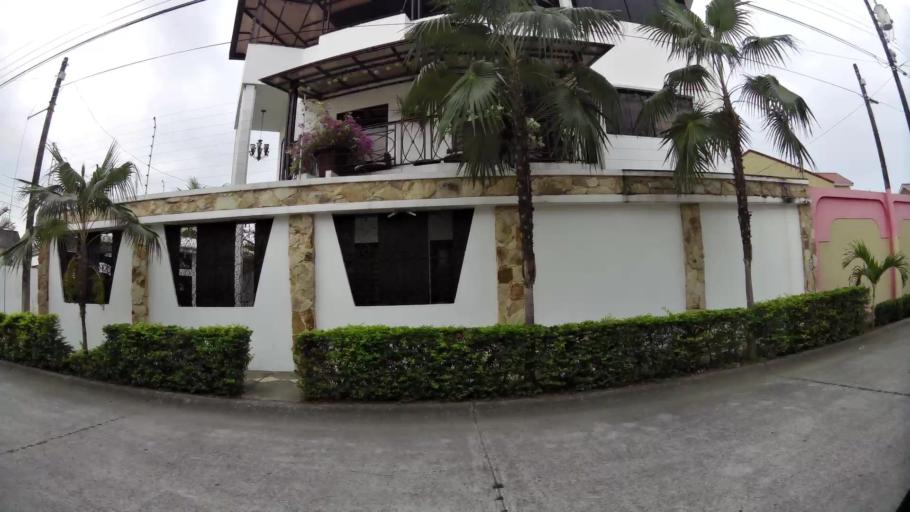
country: EC
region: Guayas
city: Eloy Alfaro
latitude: -2.1289
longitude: -79.8834
